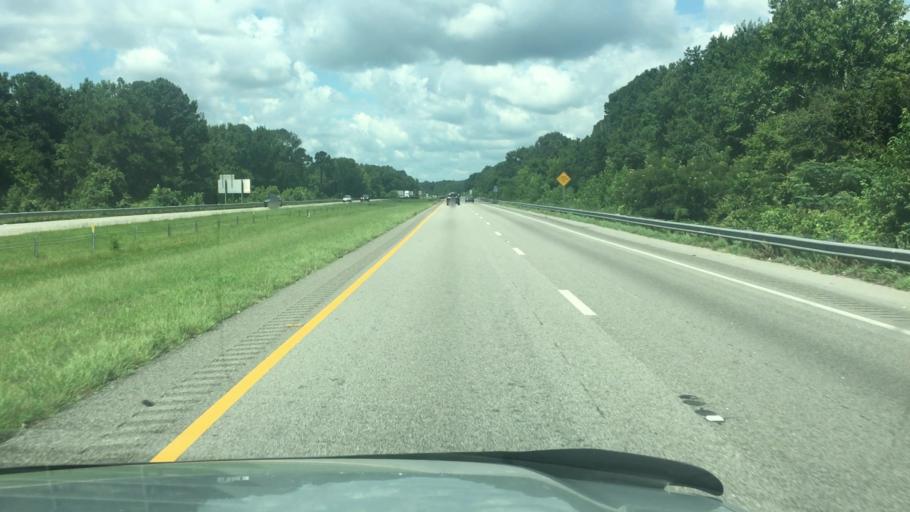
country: US
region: South Carolina
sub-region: Kershaw County
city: Camden
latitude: 34.2182
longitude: -80.6030
